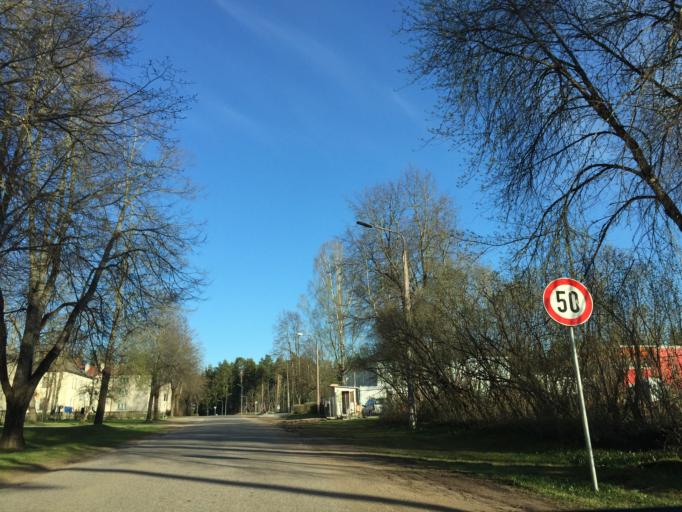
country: LV
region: Valkas Rajons
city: Valka
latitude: 57.7874
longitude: 25.9943
